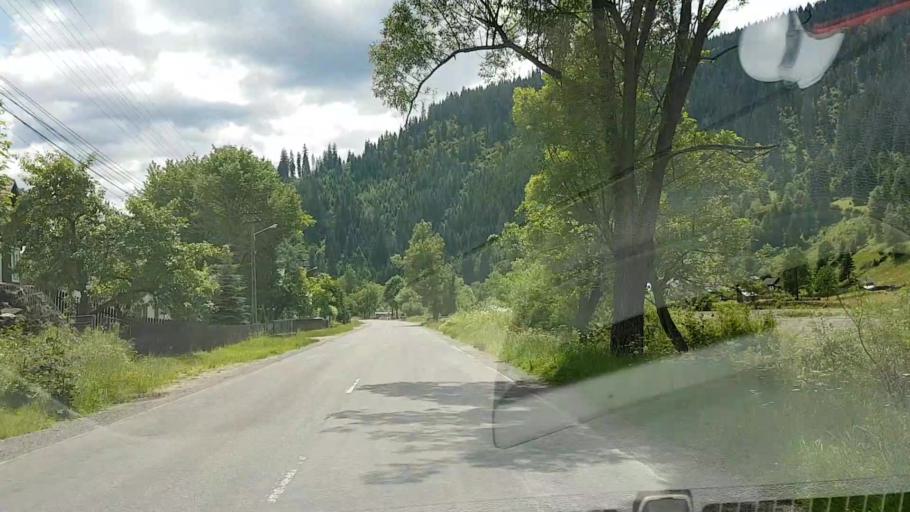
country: RO
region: Suceava
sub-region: Comuna Brosteni
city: Brosteni
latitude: 47.2435
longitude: 25.6911
